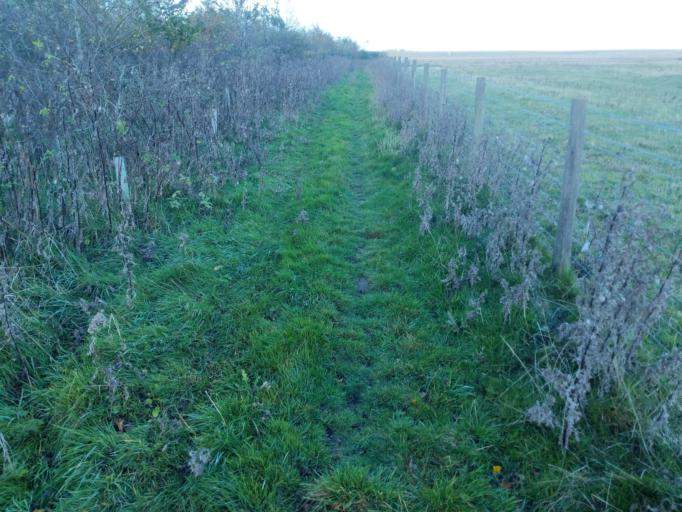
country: GB
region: England
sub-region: County Durham
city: Tow Law
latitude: 54.7310
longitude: -1.7712
